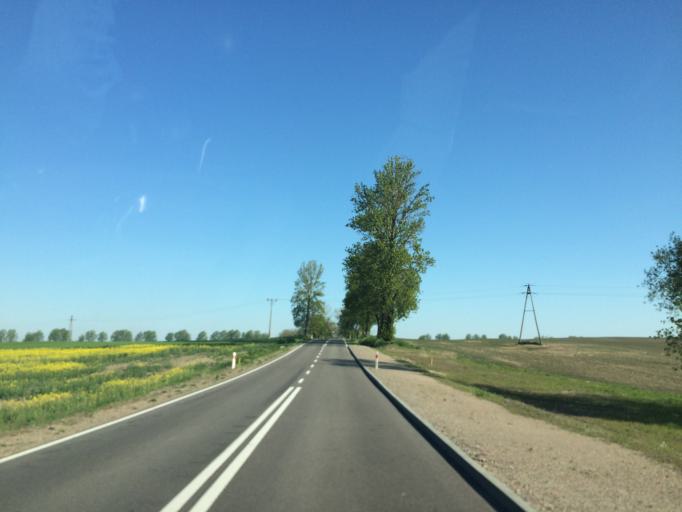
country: PL
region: Warmian-Masurian Voivodeship
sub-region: Powiat ilawski
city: Lubawa
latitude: 53.4122
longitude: 19.7930
